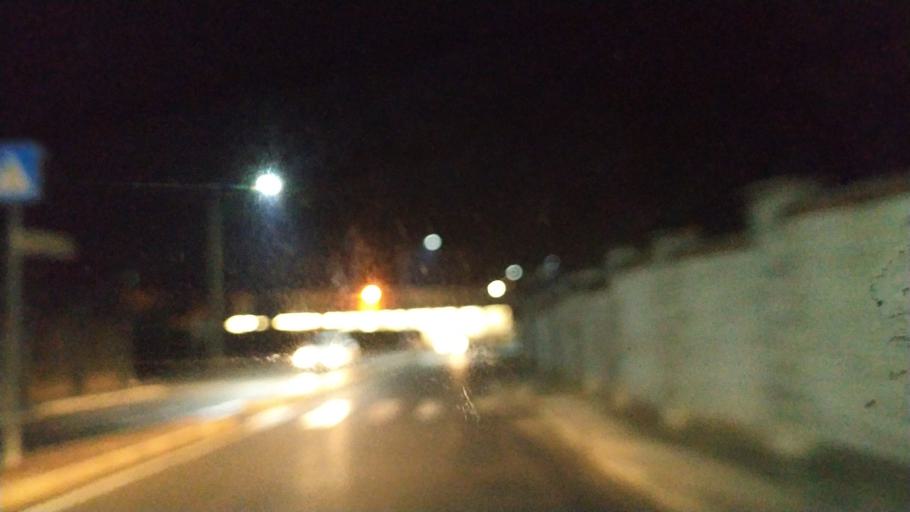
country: IT
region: Piedmont
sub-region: Provincia di Biella
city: Occhieppo Inferiore
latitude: 45.5562
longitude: 8.0195
